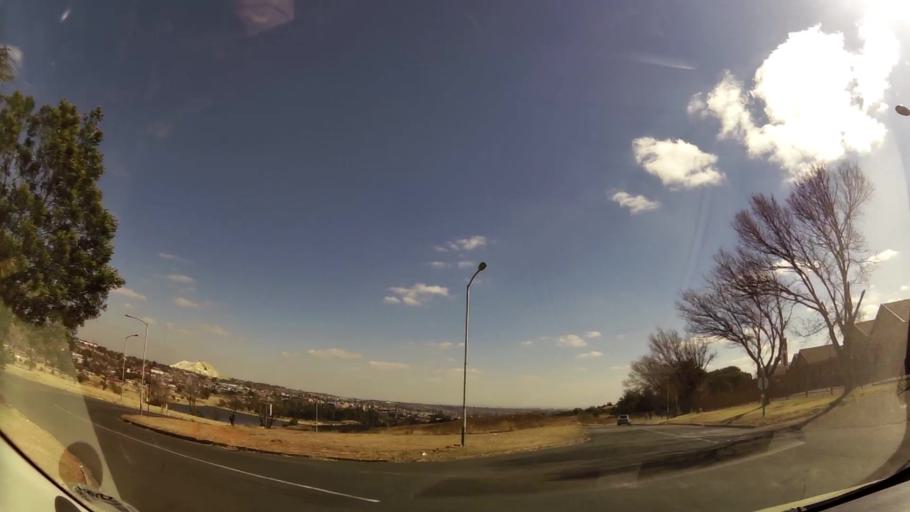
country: ZA
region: Gauteng
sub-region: West Rand District Municipality
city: Krugersdorp
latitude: -26.1020
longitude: 27.7942
